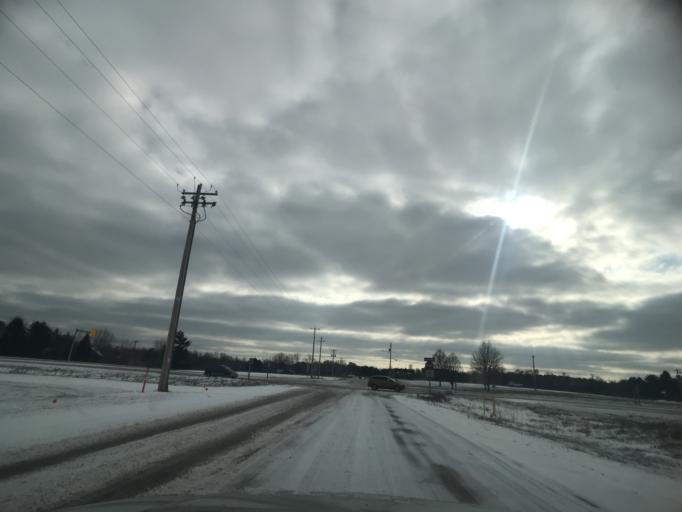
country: US
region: Wisconsin
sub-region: Door County
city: Sturgeon Bay
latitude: 44.8182
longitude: -87.3643
